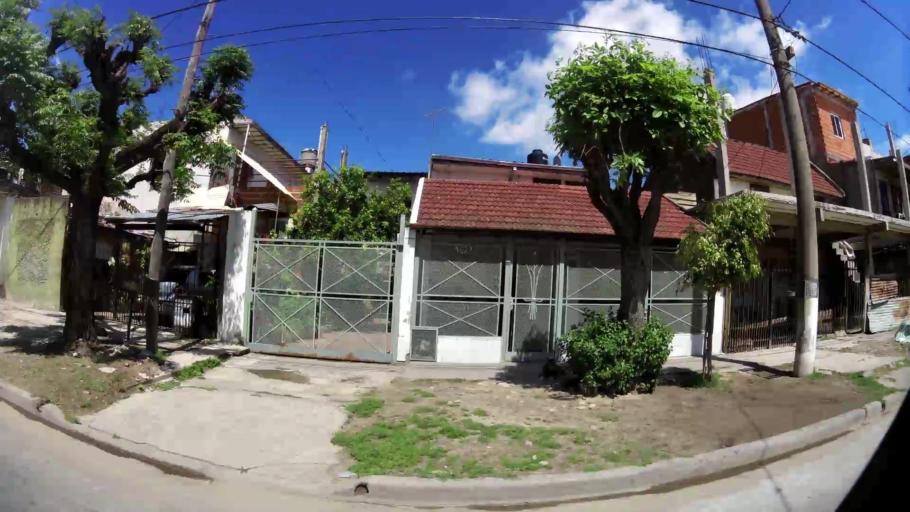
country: AR
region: Buenos Aires
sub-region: Partido de Lanus
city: Lanus
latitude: -34.6941
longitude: -58.4312
